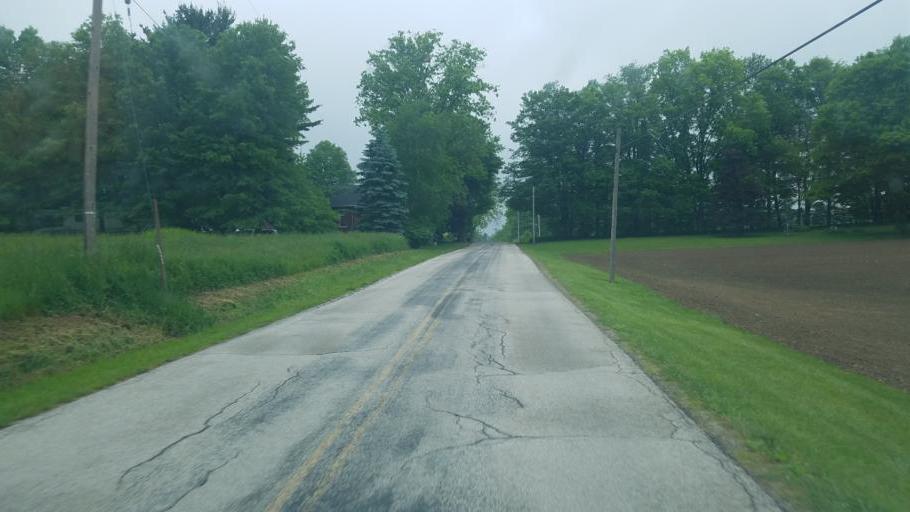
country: US
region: Ohio
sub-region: Sandusky County
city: Bellville
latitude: 40.6736
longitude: -82.4727
